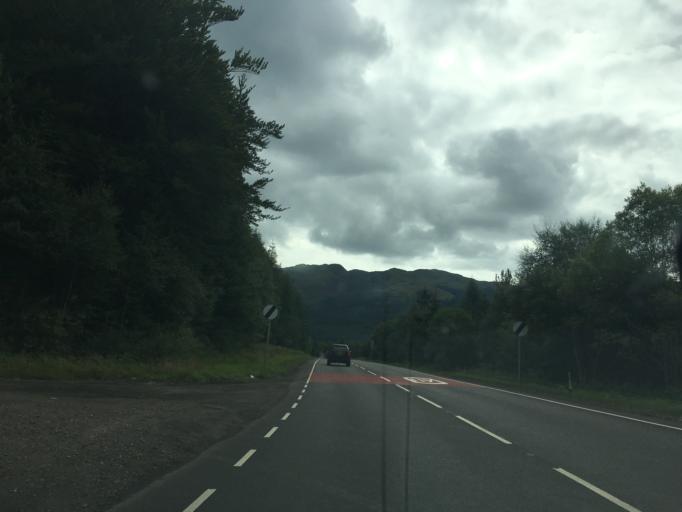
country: GB
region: Scotland
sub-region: Stirling
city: Callander
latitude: 56.3163
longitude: -4.3294
